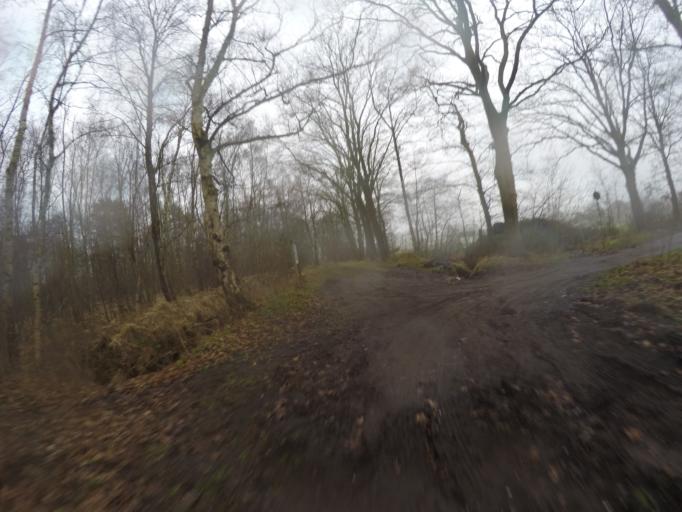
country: DE
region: Schleswig-Holstein
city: Quickborn
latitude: 53.7152
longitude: 9.9255
